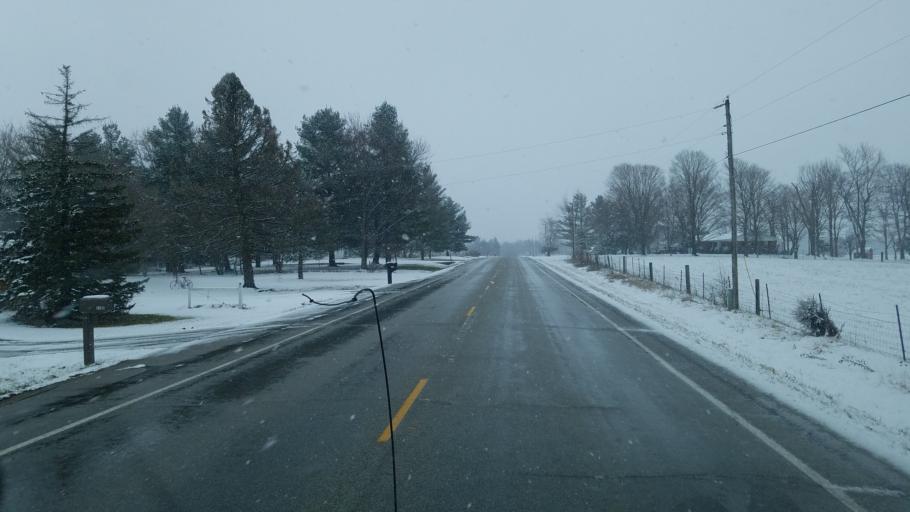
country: US
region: Indiana
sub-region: Wayne County
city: Centerville
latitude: 39.9341
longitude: -84.9731
